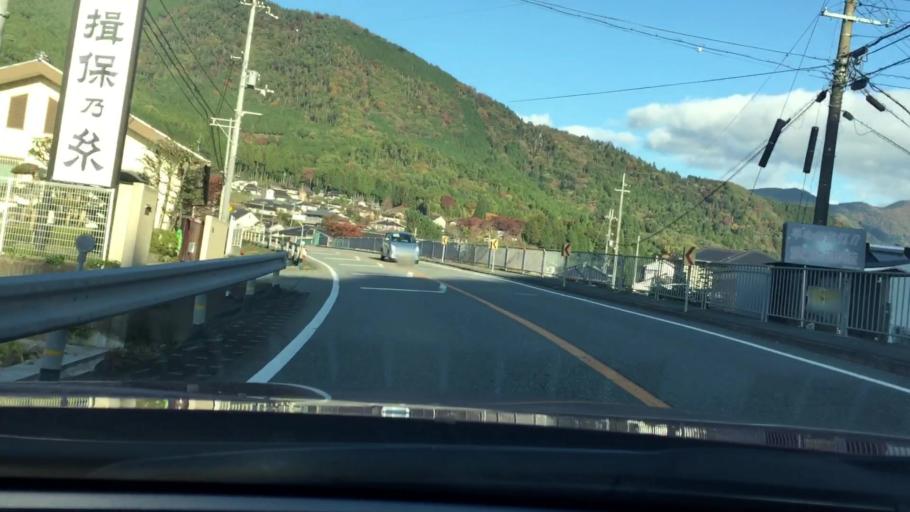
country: JP
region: Hyogo
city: Yamazakicho-nakabirose
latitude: 35.1165
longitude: 134.5703
